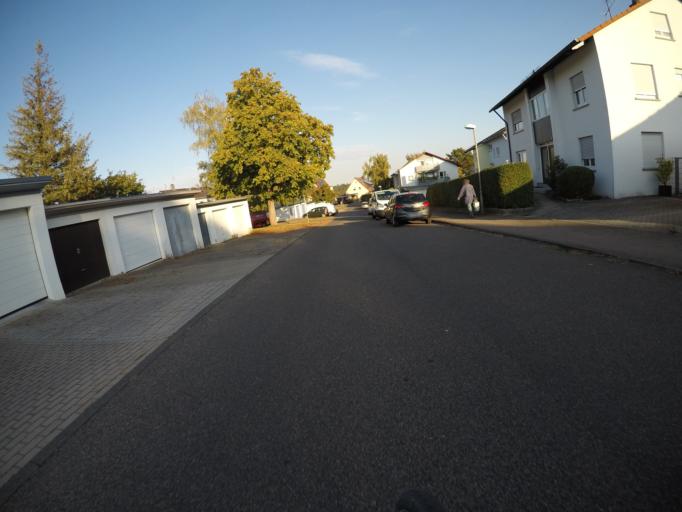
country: DE
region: Baden-Wuerttemberg
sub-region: Regierungsbezirk Stuttgart
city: Ostfildern
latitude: 48.7422
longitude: 9.2338
